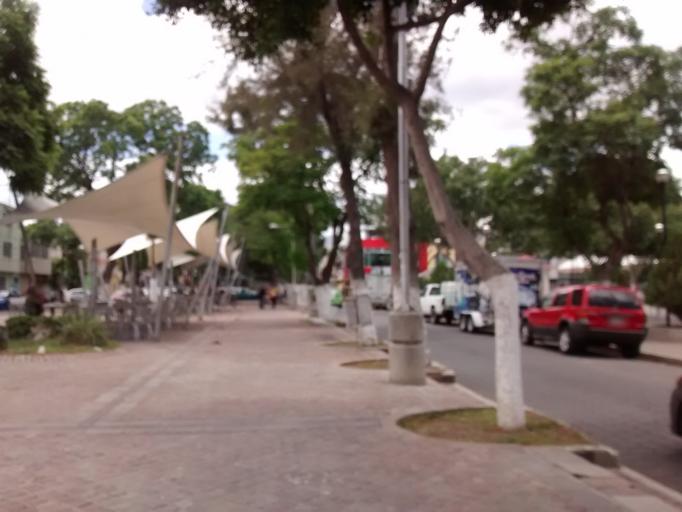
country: MX
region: Puebla
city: Tehuacan
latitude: 18.4528
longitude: -97.3927
